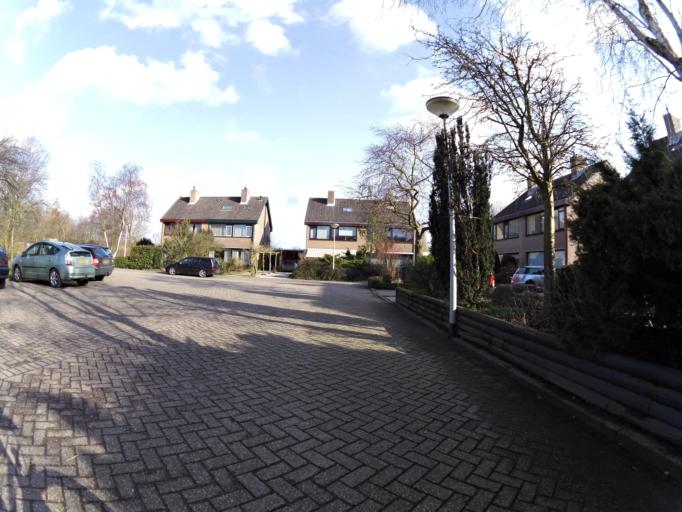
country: NL
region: South Holland
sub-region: Gemeente Brielle
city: Brielle
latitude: 51.9126
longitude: 4.1678
